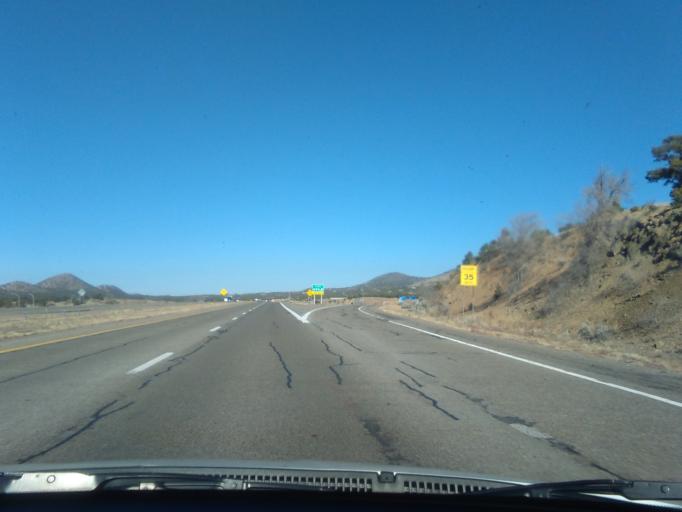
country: US
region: New Mexico
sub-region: Santa Fe County
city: Eldorado at Santa Fe
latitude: 35.5515
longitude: -105.8765
